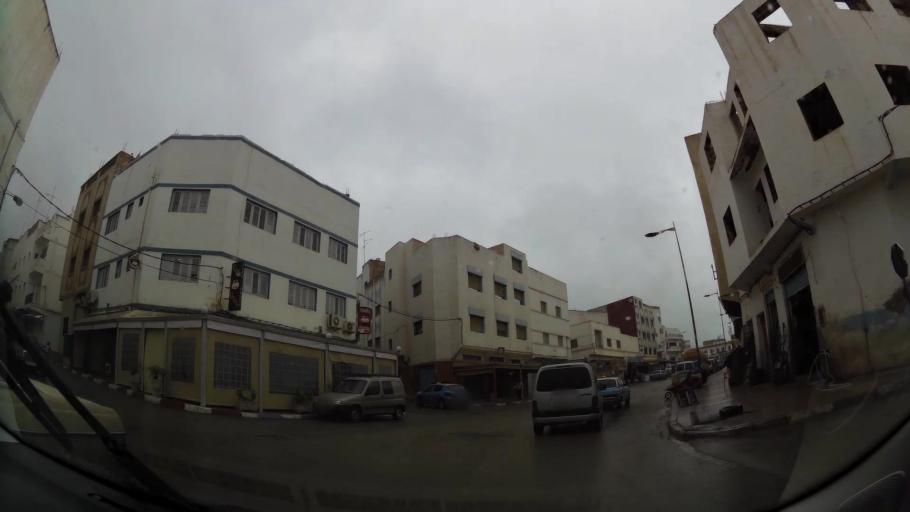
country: MA
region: Taza-Al Hoceima-Taounate
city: Imzourene
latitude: 35.1445
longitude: -3.8496
